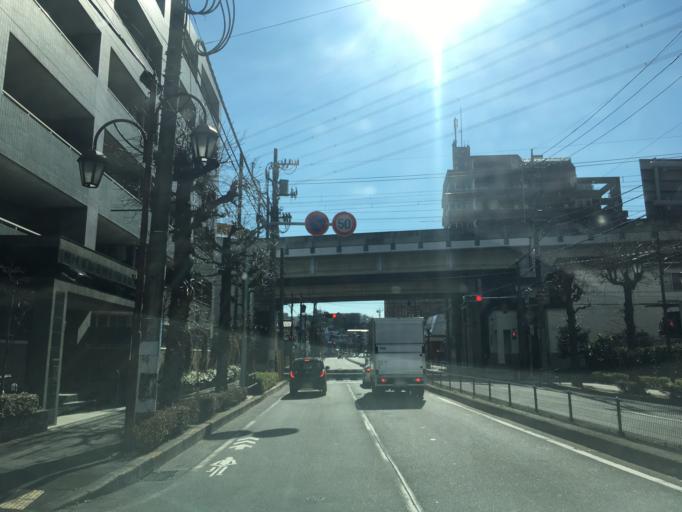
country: JP
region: Tokyo
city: Hino
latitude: 35.6276
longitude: 139.4293
